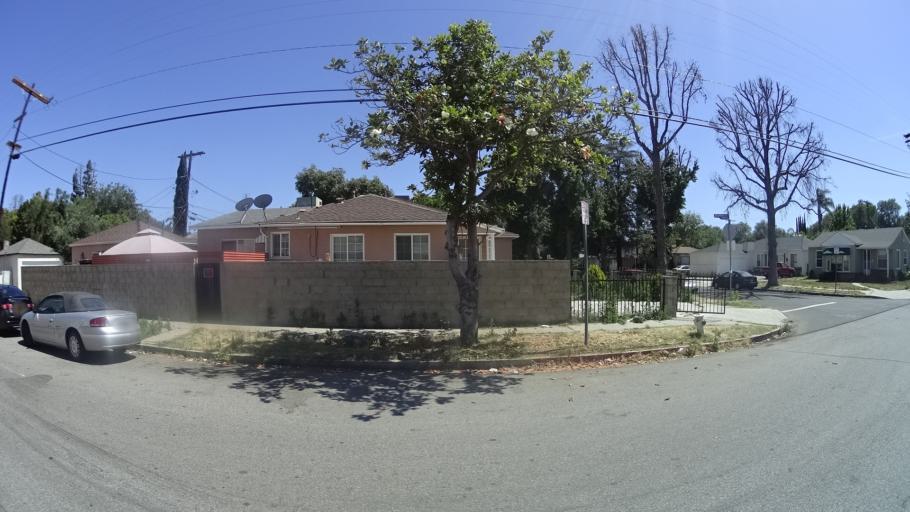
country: US
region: California
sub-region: Los Angeles County
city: Van Nuys
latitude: 34.1929
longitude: -118.4933
